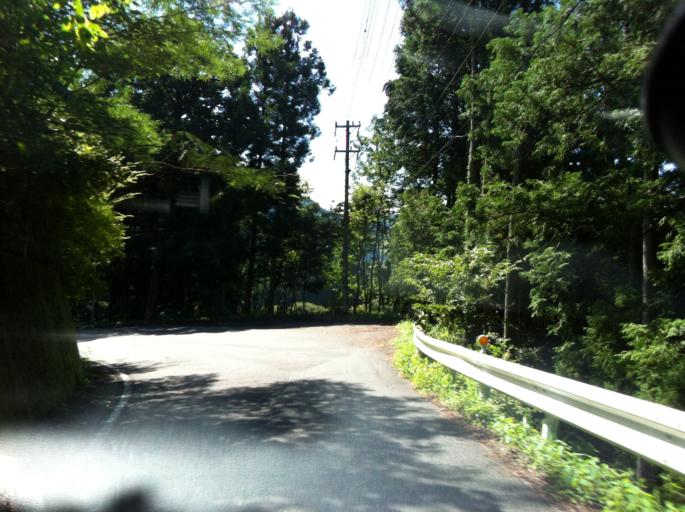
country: JP
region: Shizuoka
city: Kanaya
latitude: 35.0812
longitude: 138.1125
